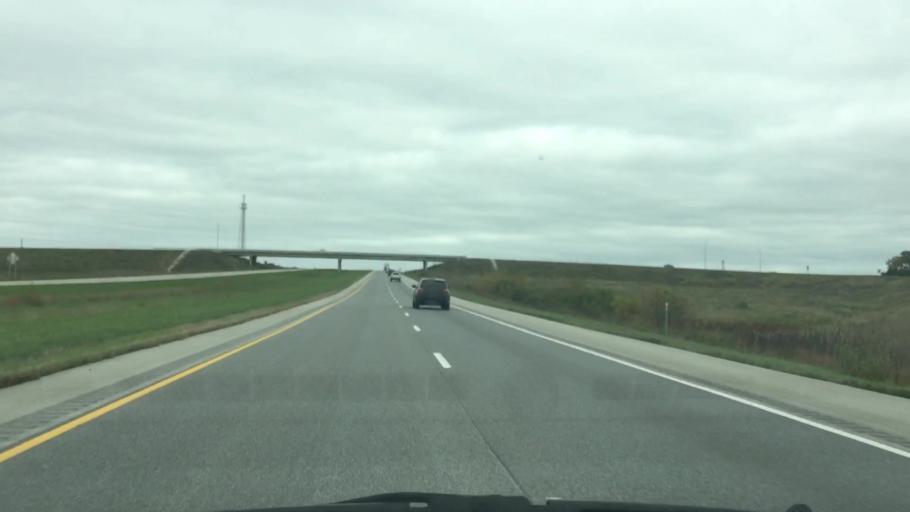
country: US
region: Iowa
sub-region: Warren County
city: Norwalk
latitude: 41.4792
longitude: -93.7800
